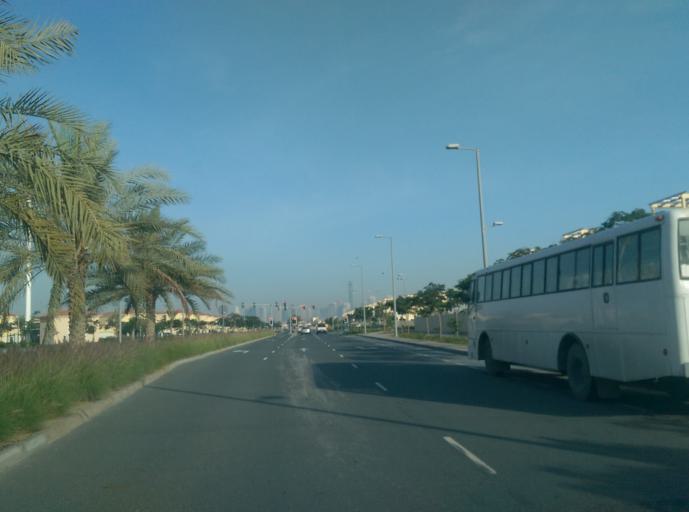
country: AE
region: Dubai
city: Dubai
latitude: 25.0405
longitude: 55.1716
